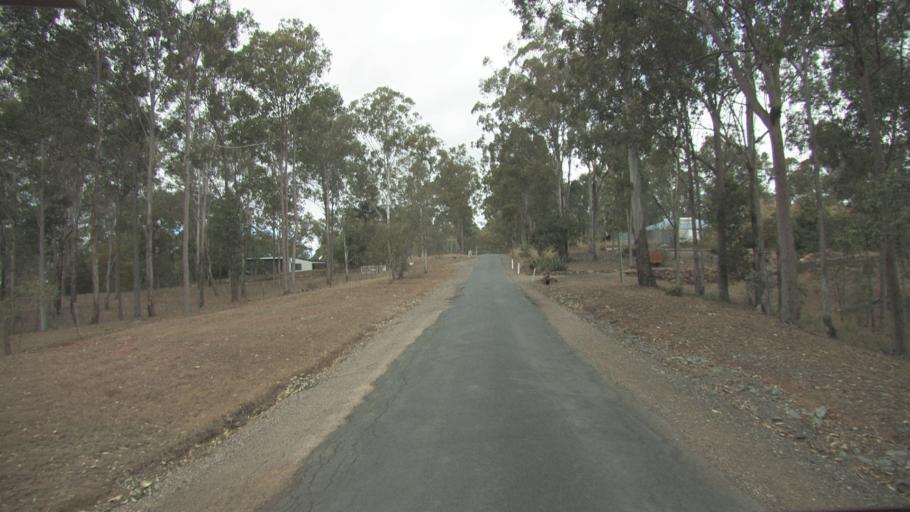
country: AU
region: Queensland
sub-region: Logan
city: Cedar Vale
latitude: -27.8918
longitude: 153.0319
